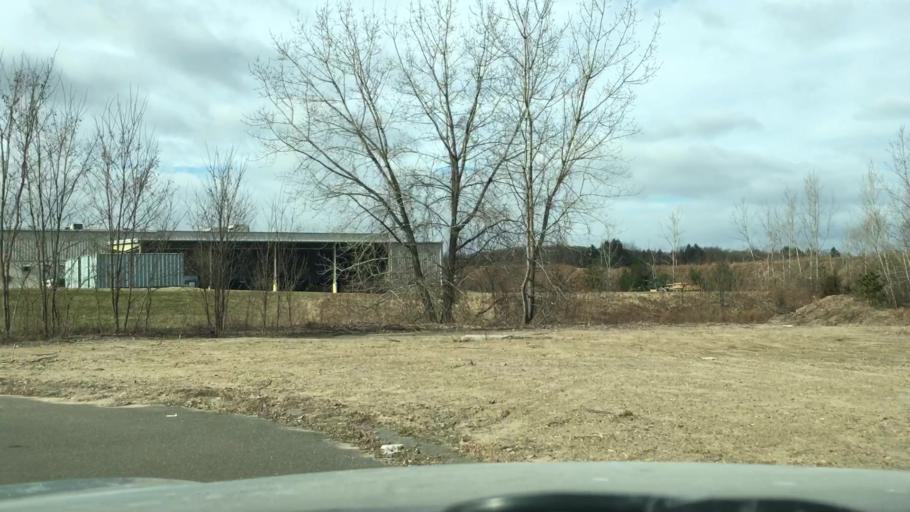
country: US
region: Massachusetts
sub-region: Hampden County
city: Southwick
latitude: 42.0696
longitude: -72.7409
